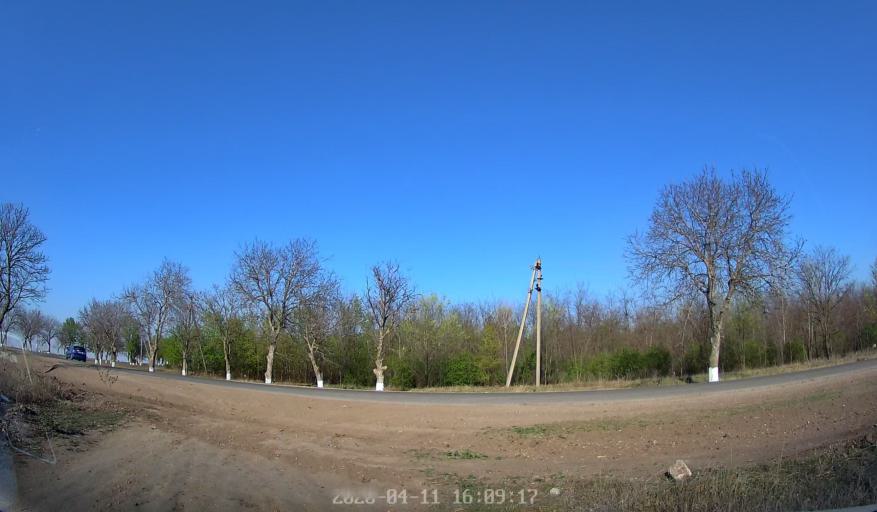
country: MD
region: Chisinau
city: Vadul lui Voda
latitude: 47.0756
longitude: 29.1363
